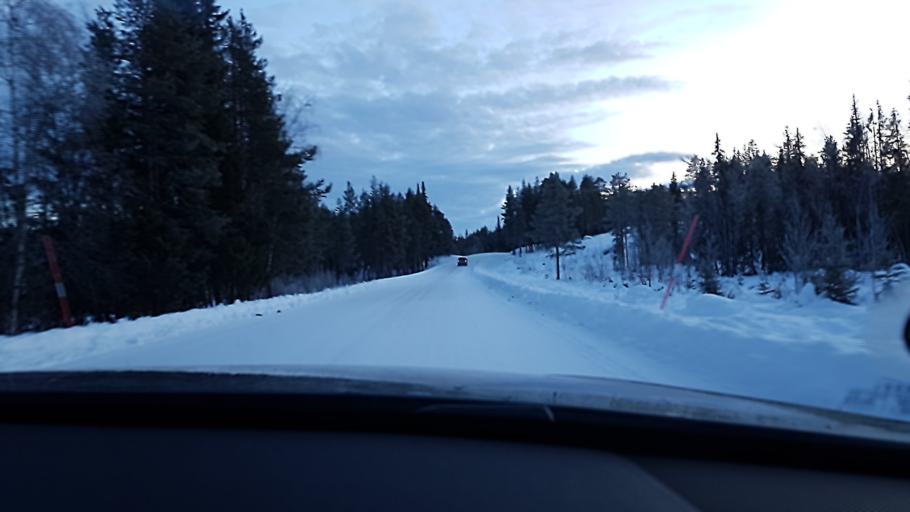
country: SE
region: Vaesterbotten
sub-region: Sorsele Kommun
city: Sorsele
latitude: 65.5014
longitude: 17.5537
